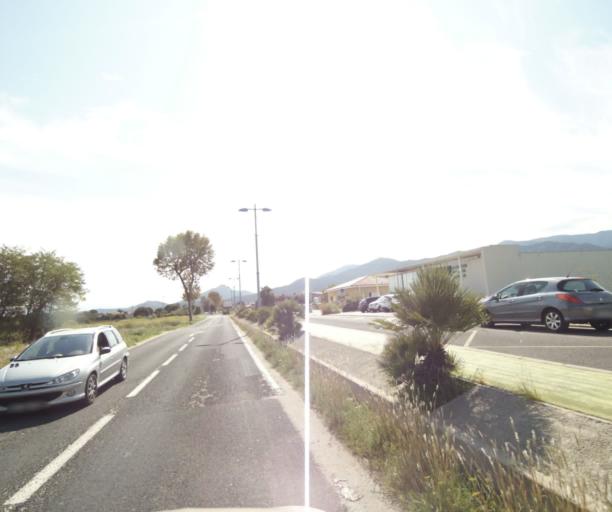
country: FR
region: Languedoc-Roussillon
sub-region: Departement des Pyrenees-Orientales
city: Argelers
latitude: 42.5570
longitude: 3.0120
